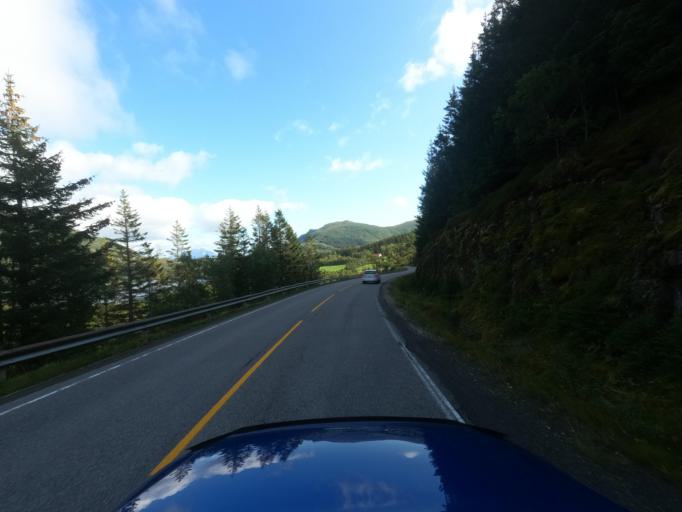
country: NO
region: Nordland
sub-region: Vestvagoy
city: Evjen
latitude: 68.1561
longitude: 13.7268
